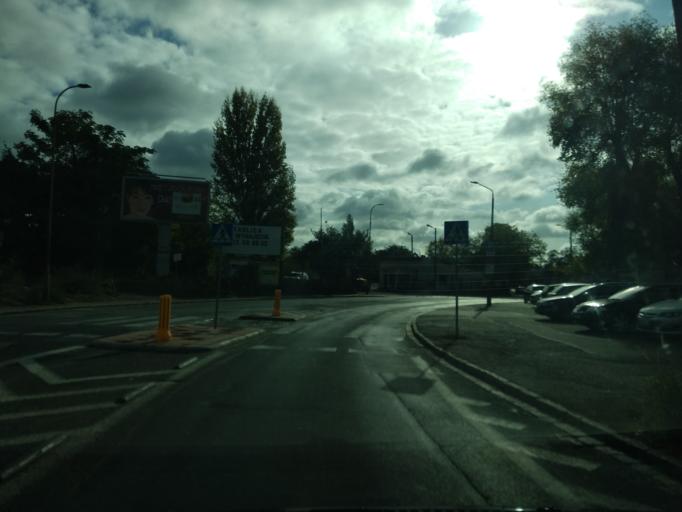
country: PL
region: Lower Silesian Voivodeship
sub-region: Powiat wroclawski
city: Wroclaw
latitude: 51.1105
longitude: 17.0067
